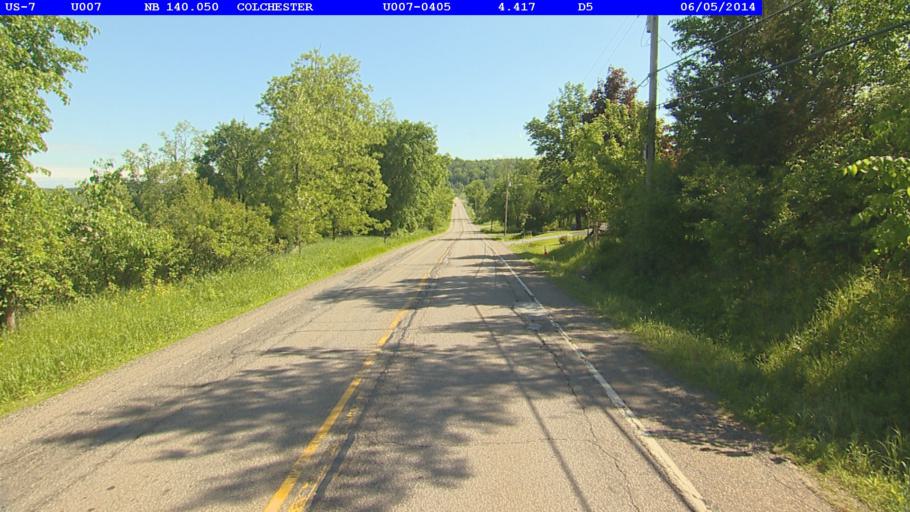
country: US
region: Vermont
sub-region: Chittenden County
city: Colchester
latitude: 44.5621
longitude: -73.1600
